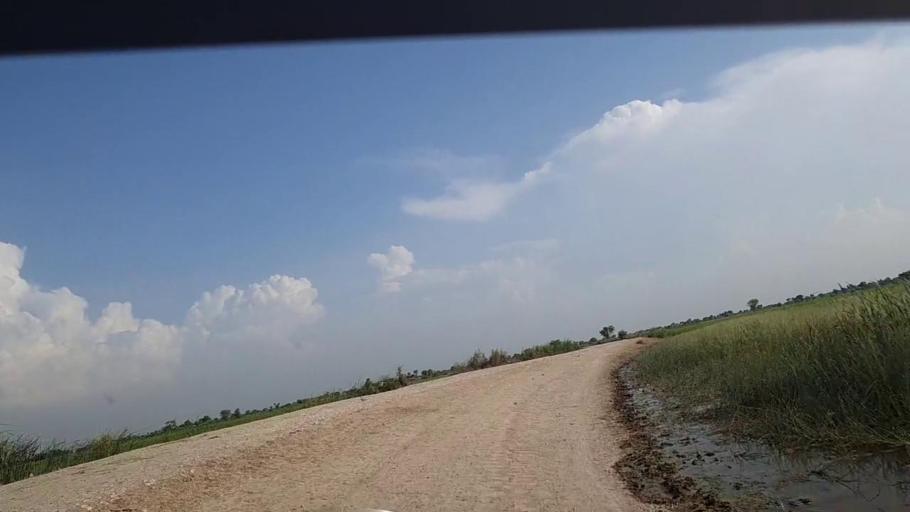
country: PK
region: Sindh
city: Khanpur
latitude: 27.8551
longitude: 69.3771
